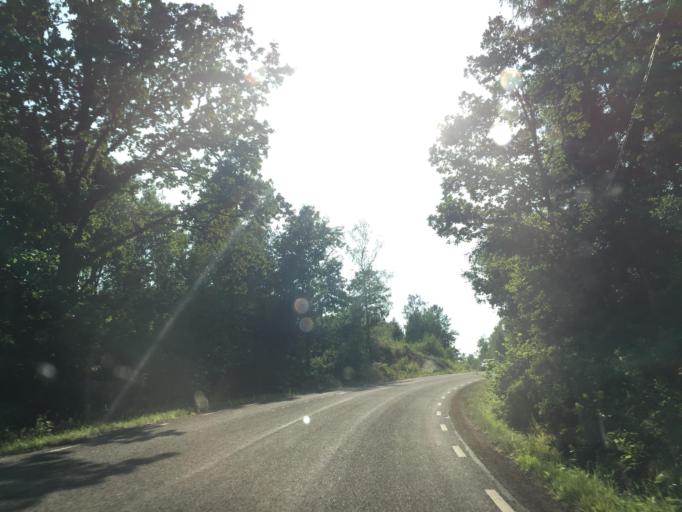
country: SE
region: Vaestra Goetaland
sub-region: Trollhattan
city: Sjuntorp
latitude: 58.2482
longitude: 12.2009
